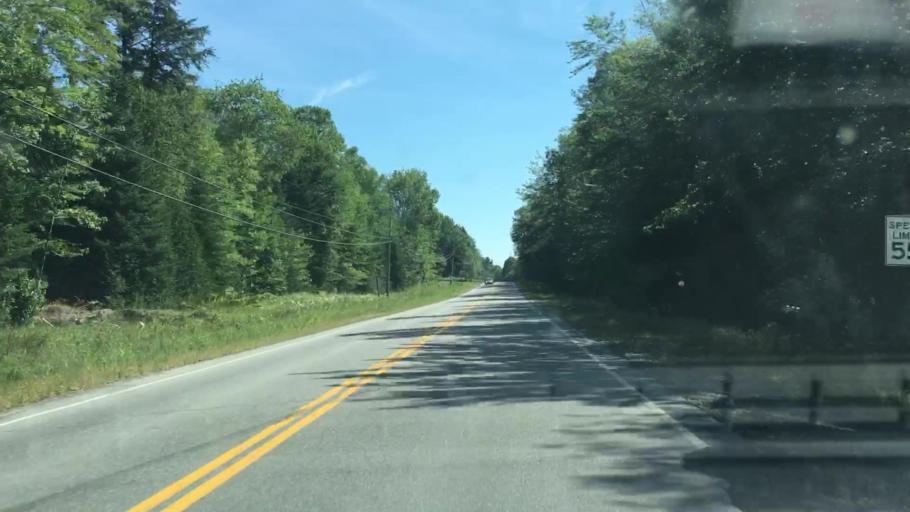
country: US
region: Maine
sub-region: Piscataquis County
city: Milo
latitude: 45.1988
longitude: -68.9054
